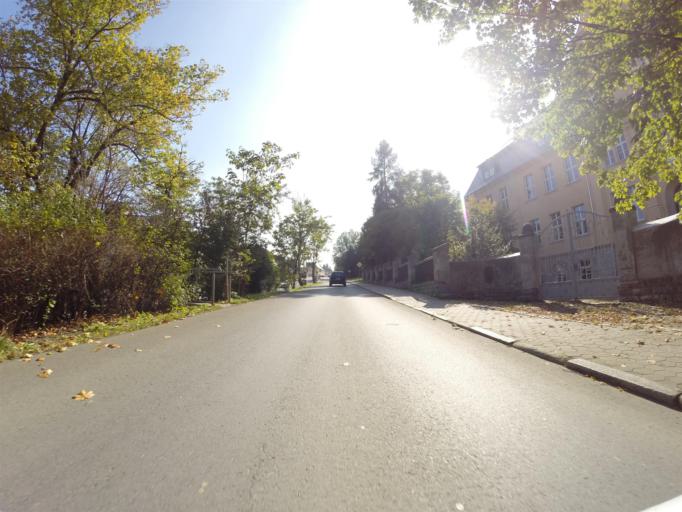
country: DE
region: Thuringia
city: Schleiz
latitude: 50.5753
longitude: 11.8087
